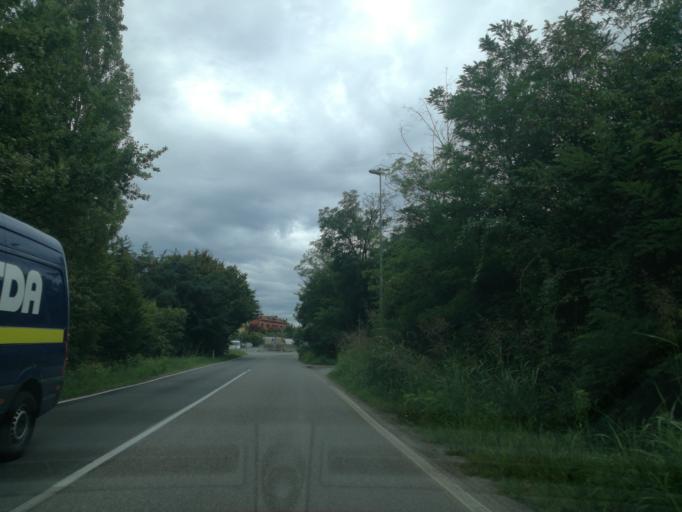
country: IT
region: Lombardy
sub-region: Provincia di Monza e Brianza
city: Mezzago
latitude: 45.6328
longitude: 9.4434
